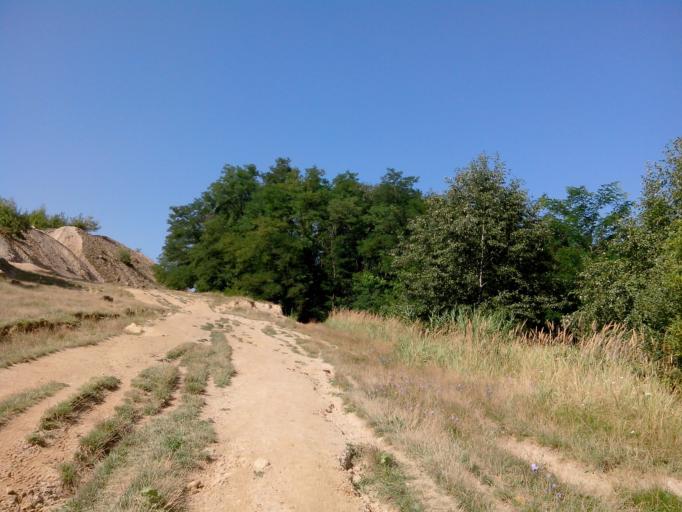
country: RO
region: Cluj
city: Aghiresu-Fabricei
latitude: 46.8911
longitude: 23.2940
